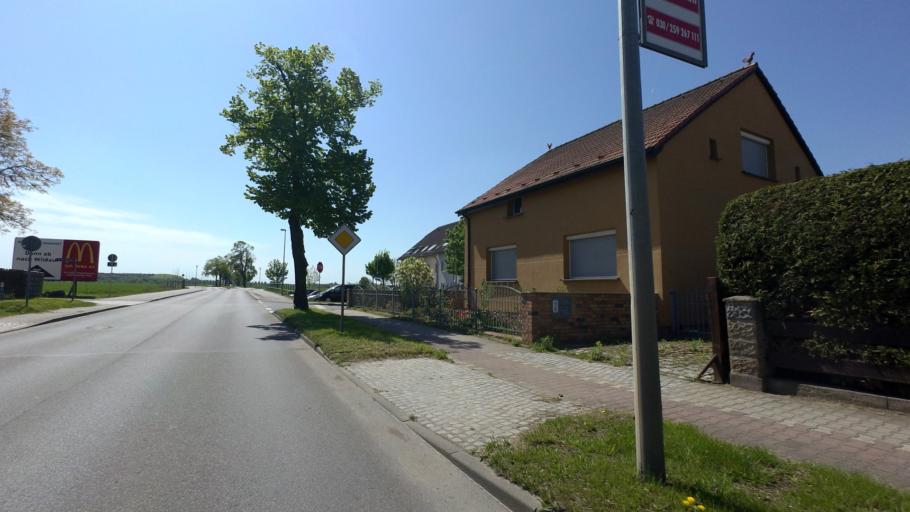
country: DE
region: Brandenburg
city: Schulzendorf
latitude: 52.3590
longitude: 13.5573
